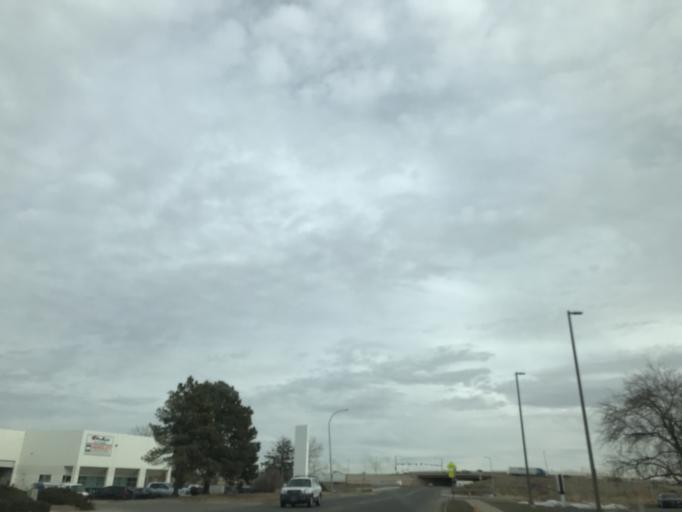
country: US
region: Colorado
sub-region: Adams County
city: Commerce City
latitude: 39.7826
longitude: -104.9045
